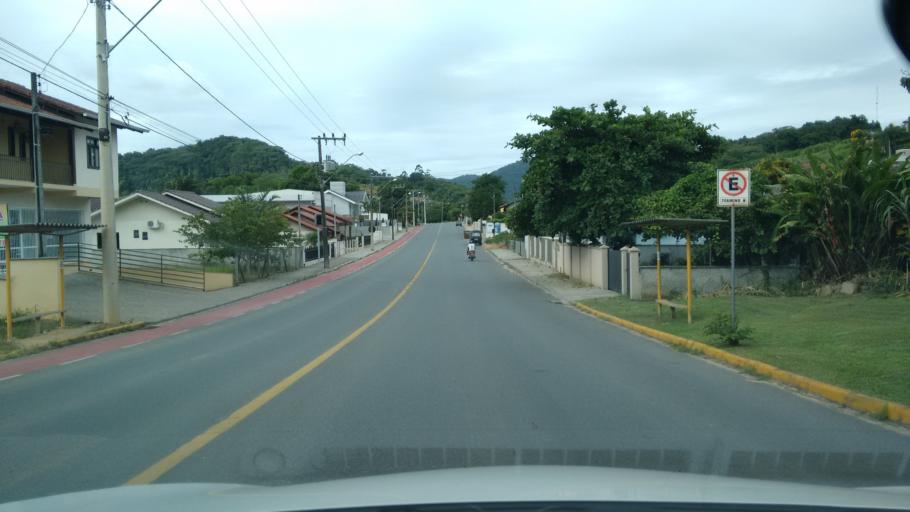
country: BR
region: Santa Catarina
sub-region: Timbo
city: Timbo
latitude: -26.8101
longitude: -49.2669
